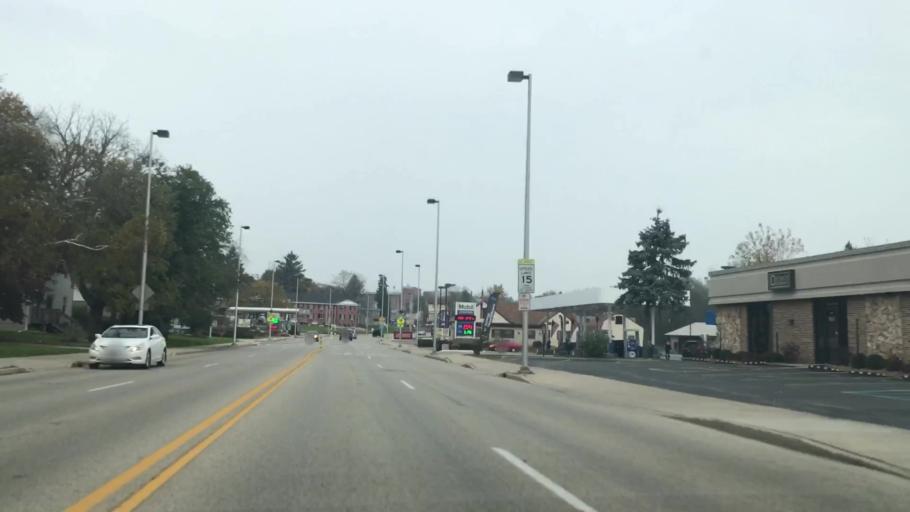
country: US
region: Wisconsin
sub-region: Waukesha County
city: Menomonee Falls
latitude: 43.1733
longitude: -88.1106
